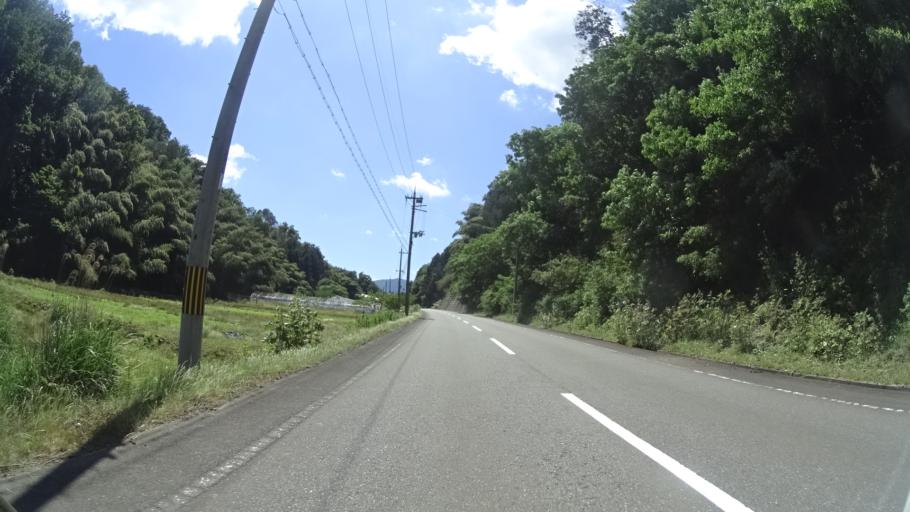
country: JP
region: Kyoto
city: Miyazu
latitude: 35.4200
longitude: 135.1752
